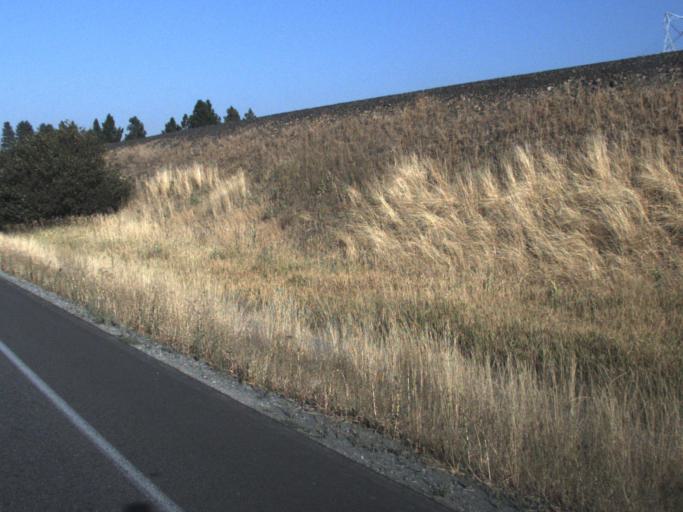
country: US
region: Washington
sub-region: Spokane County
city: Otis Orchards-East Farms
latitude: 47.7189
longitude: -117.0810
